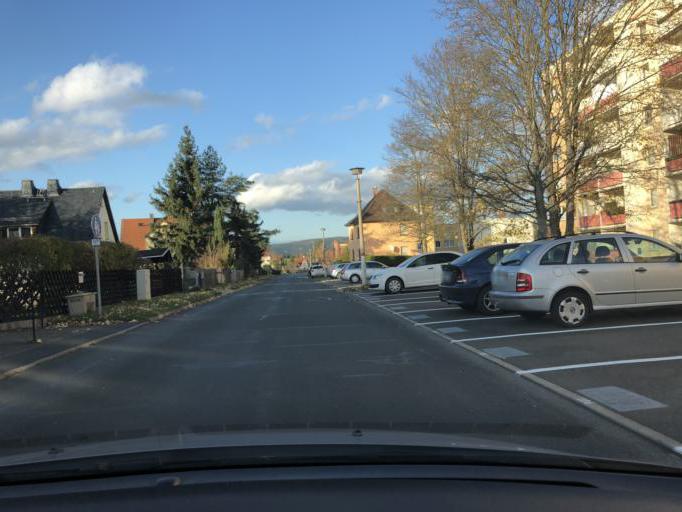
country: DE
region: Thuringia
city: Bodelwitz
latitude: 50.6974
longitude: 11.6108
